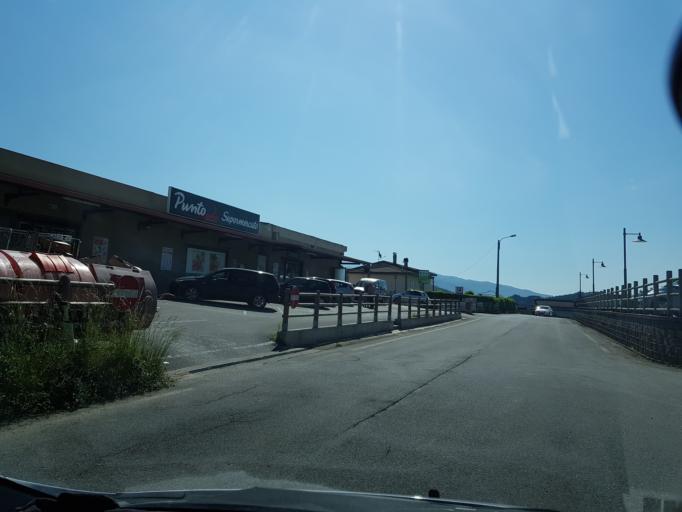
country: IT
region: Tuscany
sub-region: Provincia di Lucca
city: Camporgiano
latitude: 44.1625
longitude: 10.3301
